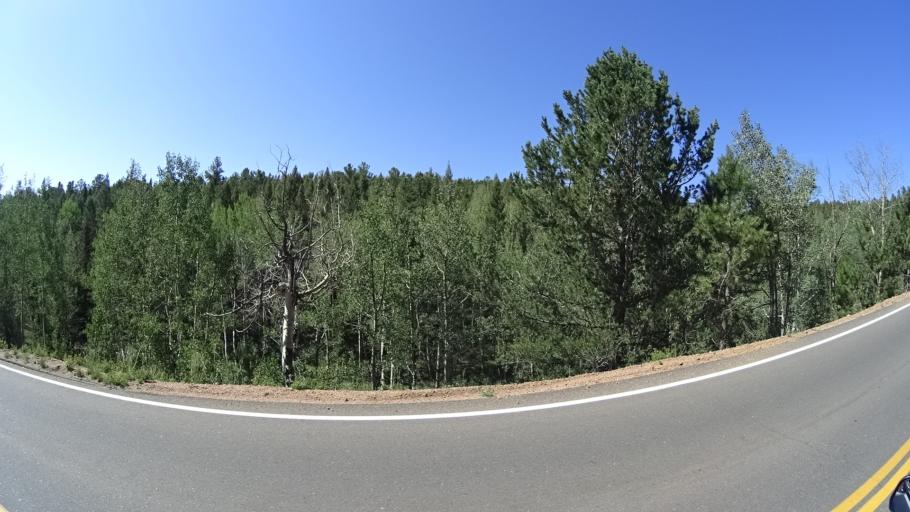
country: US
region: Colorado
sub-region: El Paso County
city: Cascade-Chipita Park
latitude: 38.9126
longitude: -105.0299
